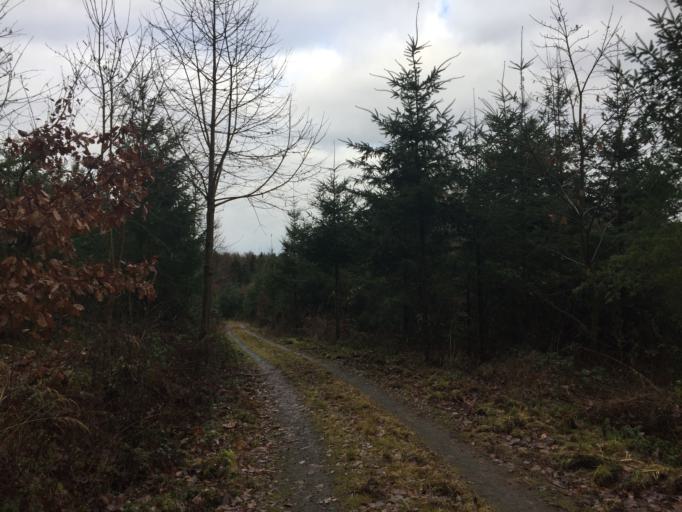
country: DE
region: Hesse
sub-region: Regierungsbezirk Giessen
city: Lich
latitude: 50.5353
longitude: 8.7946
